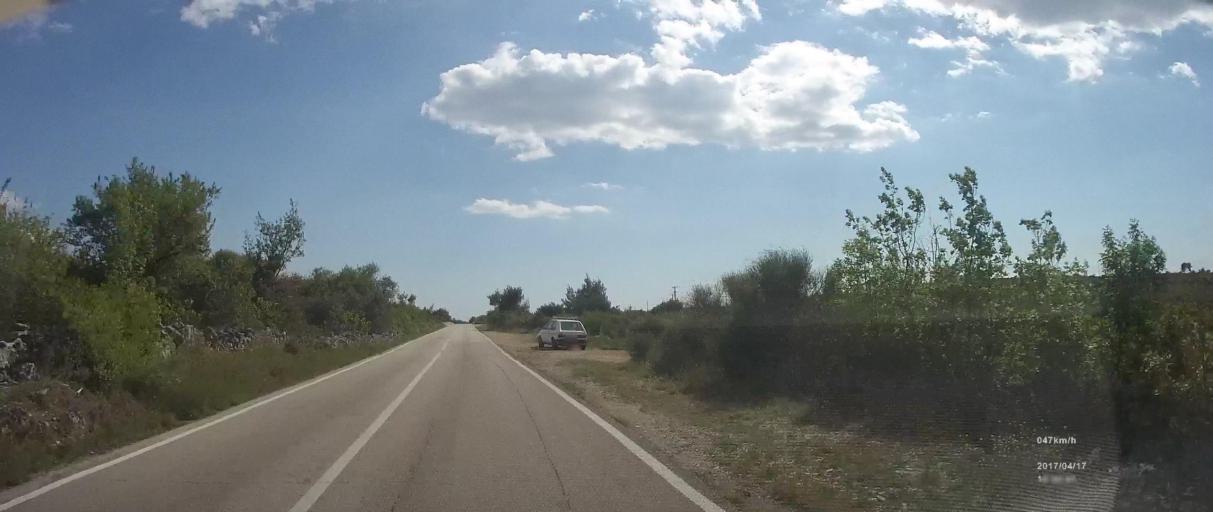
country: HR
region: Sibensko-Kniniska
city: Primosten
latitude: 43.6069
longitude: 15.9703
